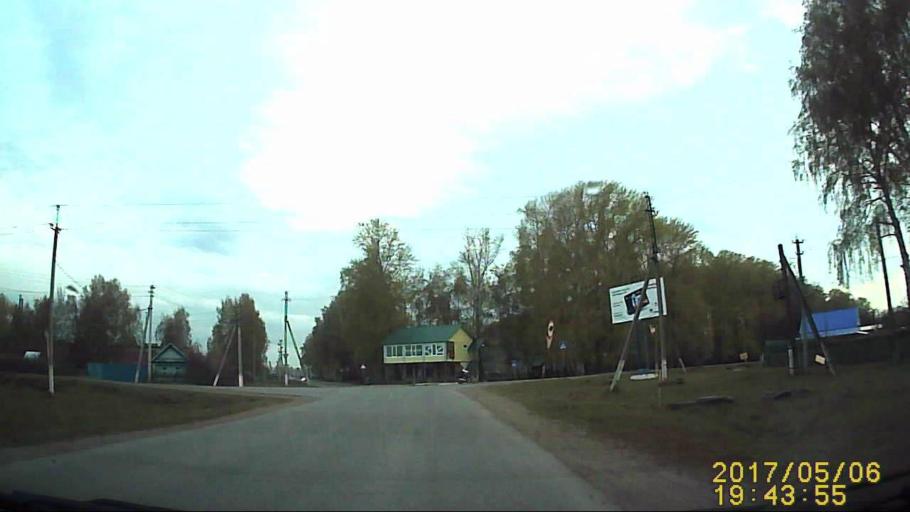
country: RU
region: Ulyanovsk
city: Staraya Mayna
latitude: 54.6079
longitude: 48.9325
